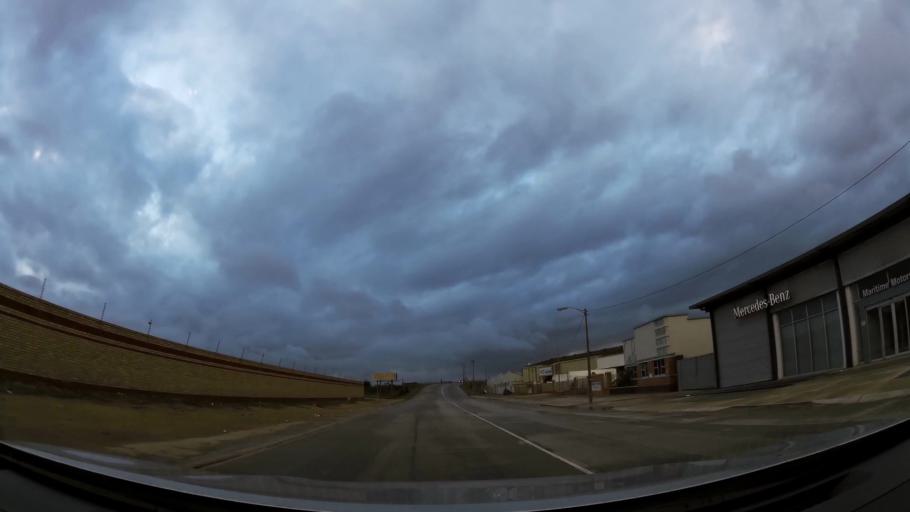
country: ZA
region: Eastern Cape
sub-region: Nelson Mandela Bay Metropolitan Municipality
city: Port Elizabeth
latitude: -33.9276
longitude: 25.6046
